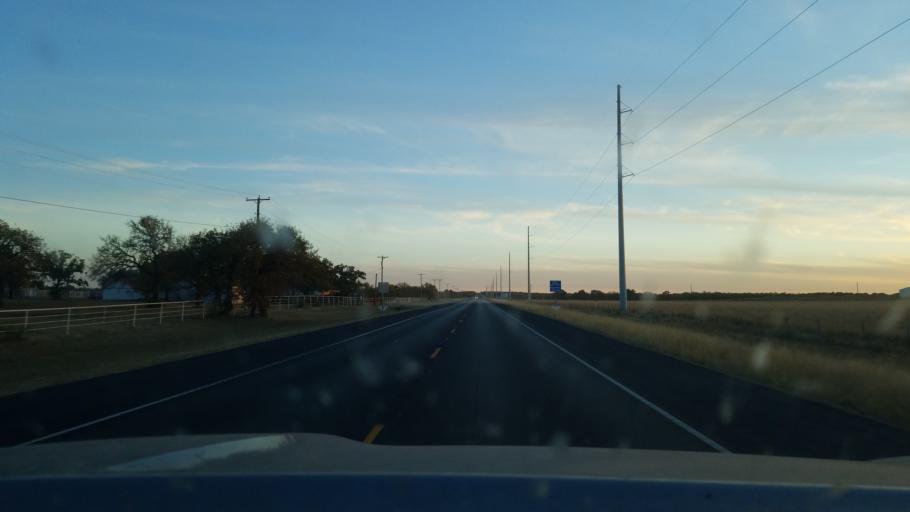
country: US
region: Texas
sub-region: Stephens County
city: Breckenridge
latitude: 32.7183
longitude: -98.9026
